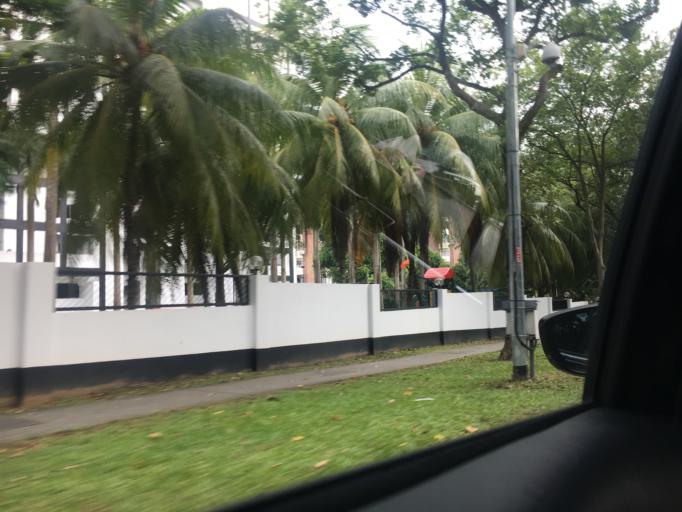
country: SG
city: Singapore
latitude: 1.3087
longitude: 103.8427
